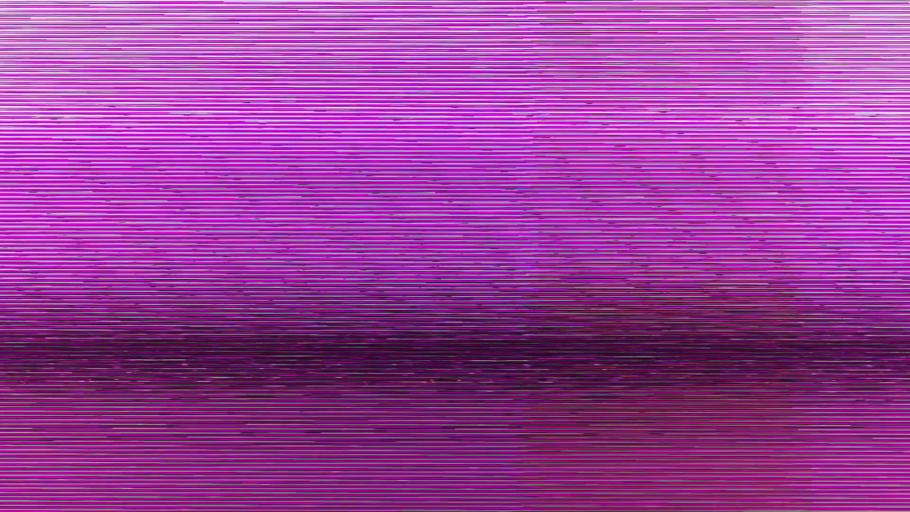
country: US
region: Michigan
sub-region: Oakland County
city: Waterford
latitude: 42.6605
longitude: -83.4317
